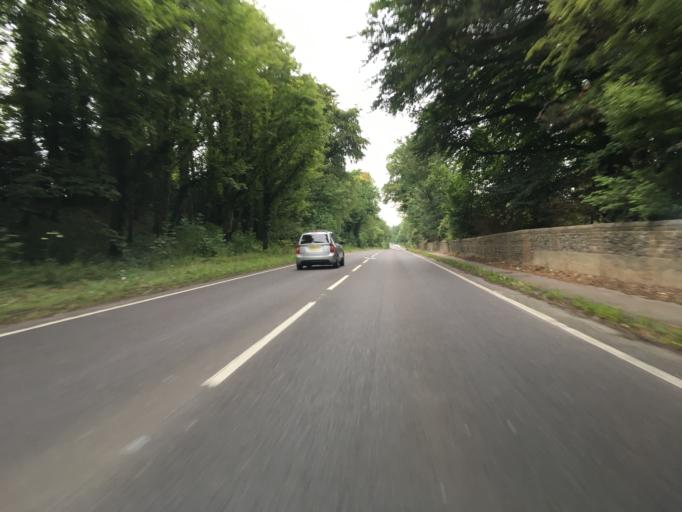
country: GB
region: England
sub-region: Hertfordshire
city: Markyate
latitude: 51.8417
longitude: -0.4665
